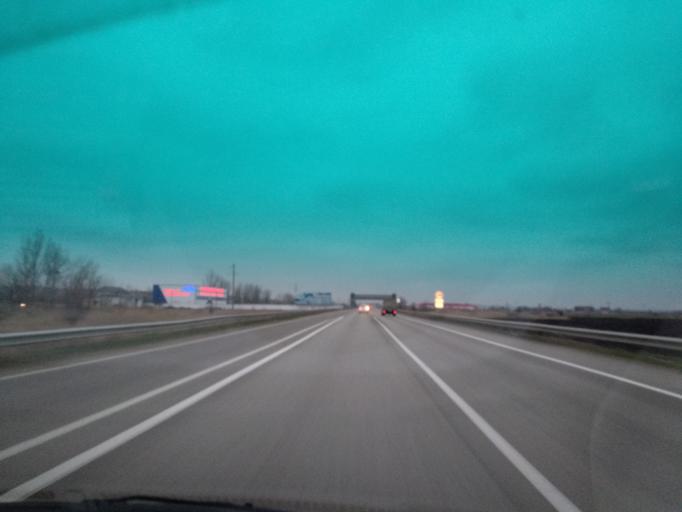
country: RU
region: Adygeya
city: Adygeysk
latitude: 44.8847
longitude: 39.1743
